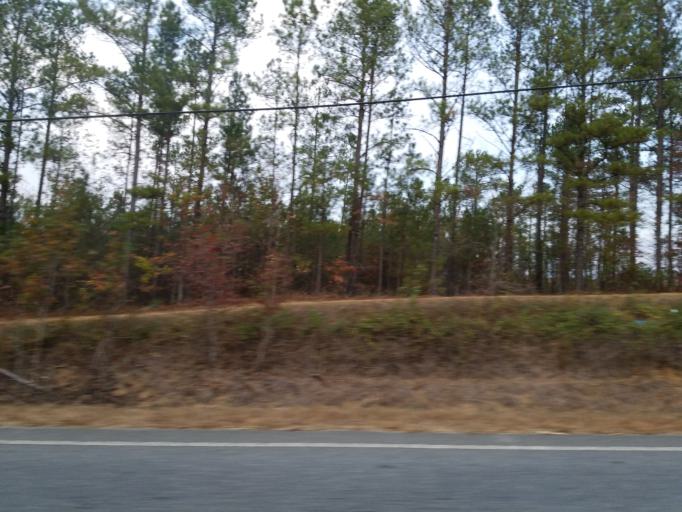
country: US
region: Georgia
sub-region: Murray County
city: Chatsworth
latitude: 34.6059
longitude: -84.8058
